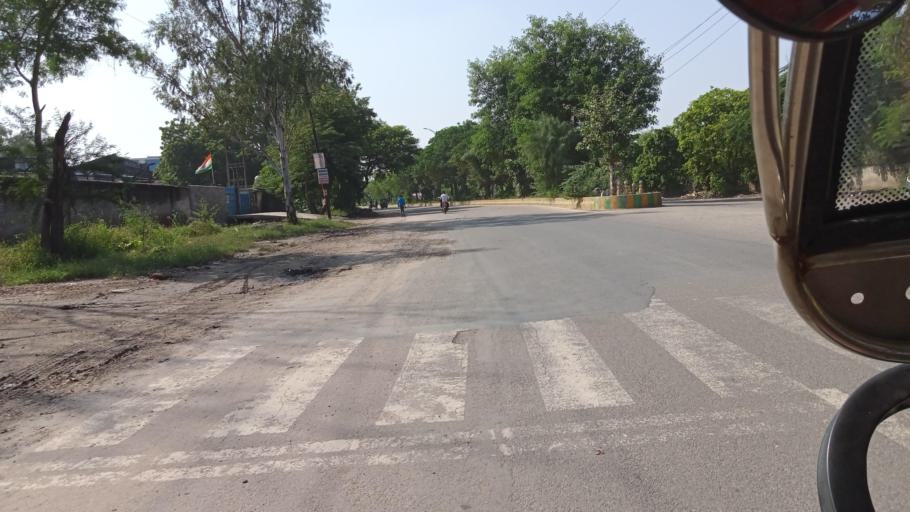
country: IN
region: Uttar Pradesh
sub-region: Ghaziabad
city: Ghaziabad
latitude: 28.6713
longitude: 77.3656
